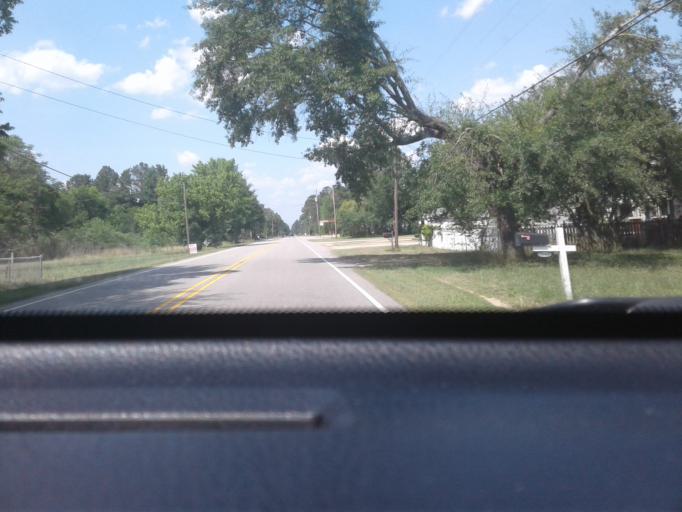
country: US
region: North Carolina
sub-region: Cumberland County
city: Eastover
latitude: 35.1650
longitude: -78.7265
